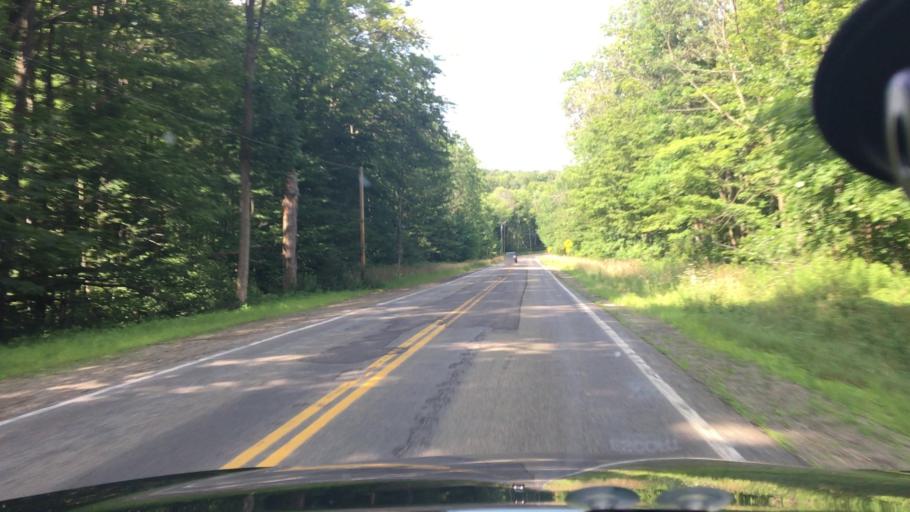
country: US
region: New York
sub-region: Chautauqua County
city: Lakewood
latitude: 42.2500
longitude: -79.3564
